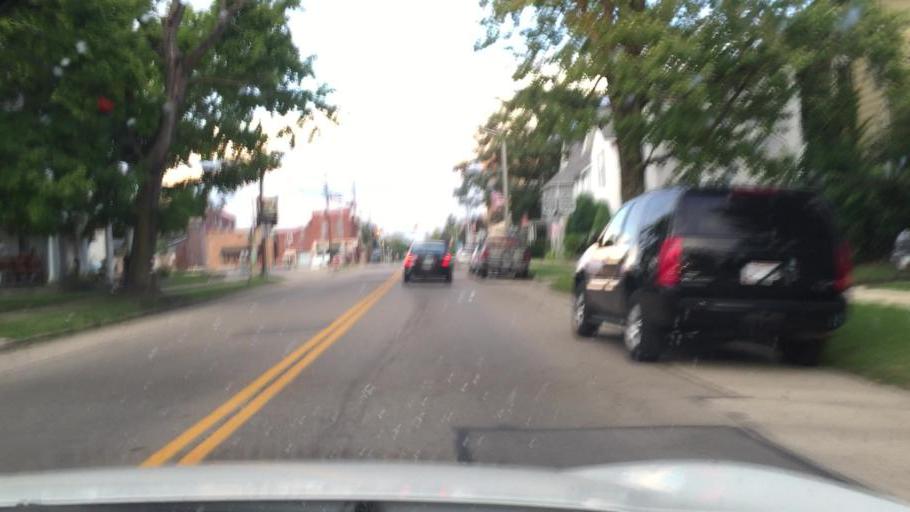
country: US
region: Ohio
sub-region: Champaign County
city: Mechanicsburg
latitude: 40.0712
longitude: -83.5571
